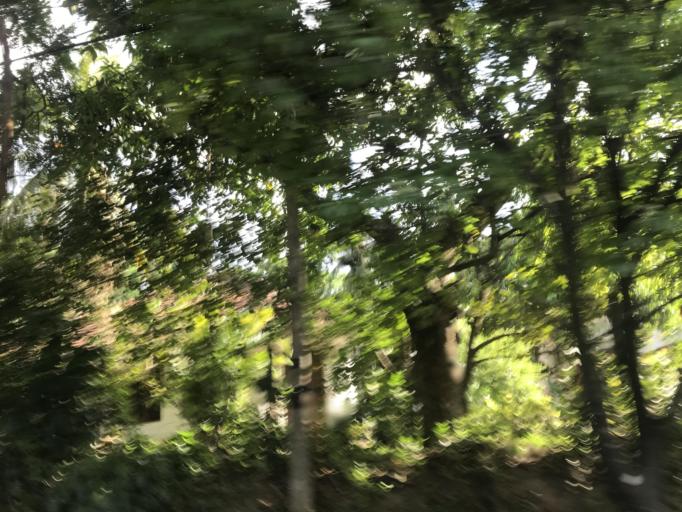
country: LK
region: Western
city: Gampaha
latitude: 7.0650
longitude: 80.0083
